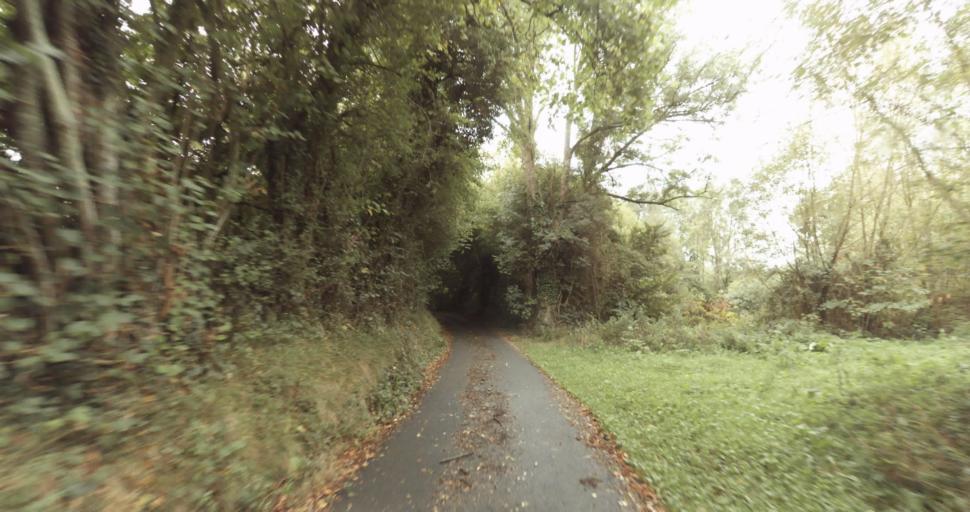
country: FR
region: Lower Normandy
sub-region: Departement de l'Orne
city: Vimoutiers
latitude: 48.9058
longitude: 0.1958
